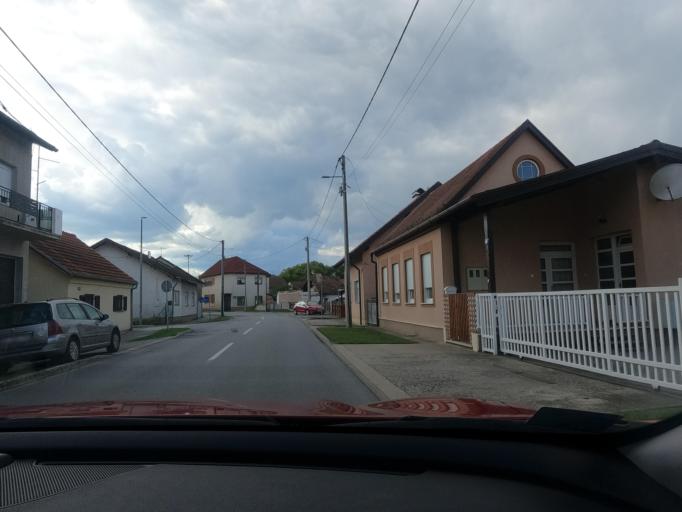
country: HR
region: Sisacko-Moslavacka
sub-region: Grad Sisak
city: Sisak
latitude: 45.4865
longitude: 16.3823
